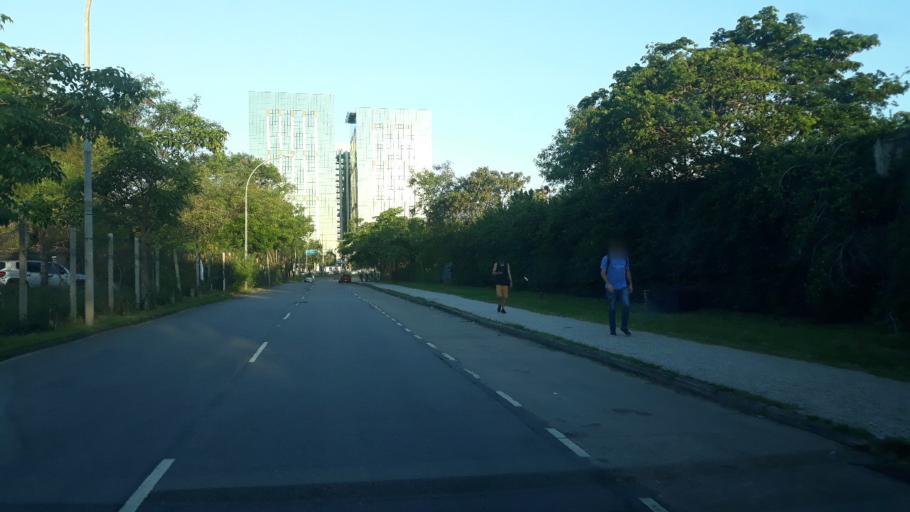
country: BR
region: Rio de Janeiro
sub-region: Rio De Janeiro
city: Rio de Janeiro
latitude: -22.9848
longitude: -43.3622
